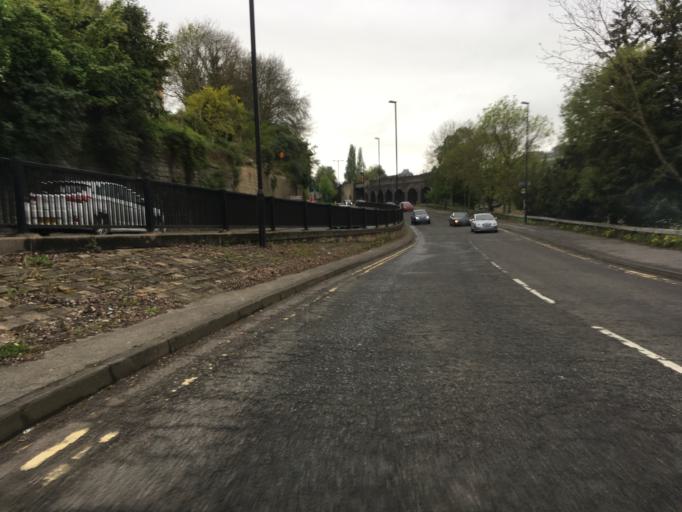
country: GB
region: England
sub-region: Bath and North East Somerset
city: Bath
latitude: 51.3768
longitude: -2.3572
